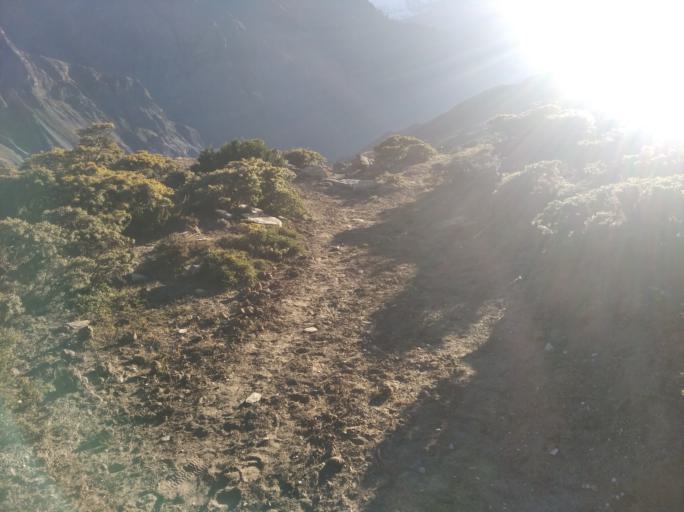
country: NP
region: Western Region
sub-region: Dhawalagiri Zone
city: Jomsom
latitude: 28.8835
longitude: 83.3566
